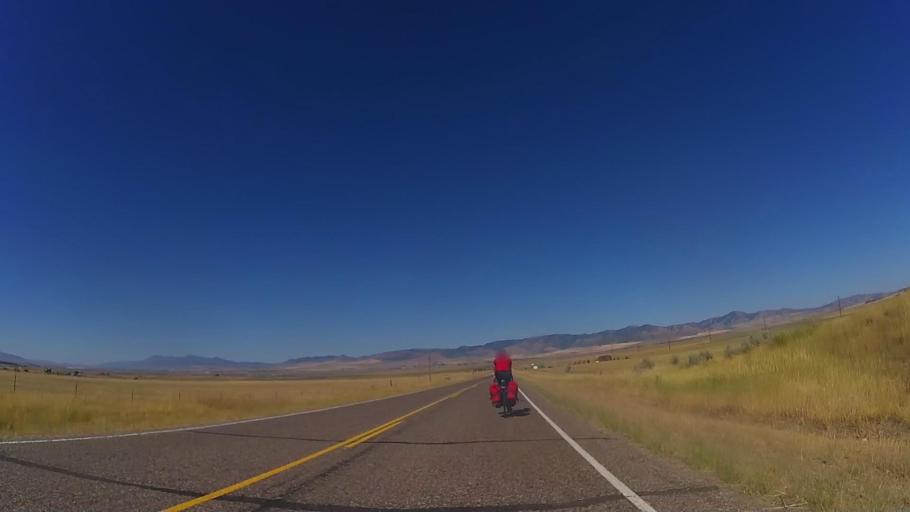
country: US
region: Idaho
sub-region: Oneida County
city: Malad City
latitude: 42.3760
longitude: -112.2074
